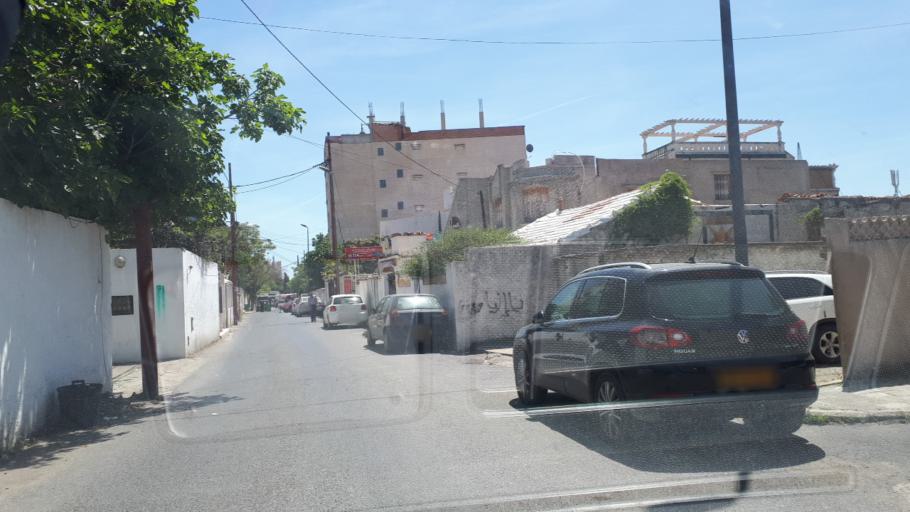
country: DZ
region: Alger
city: Algiers
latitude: 36.7485
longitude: 3.0566
